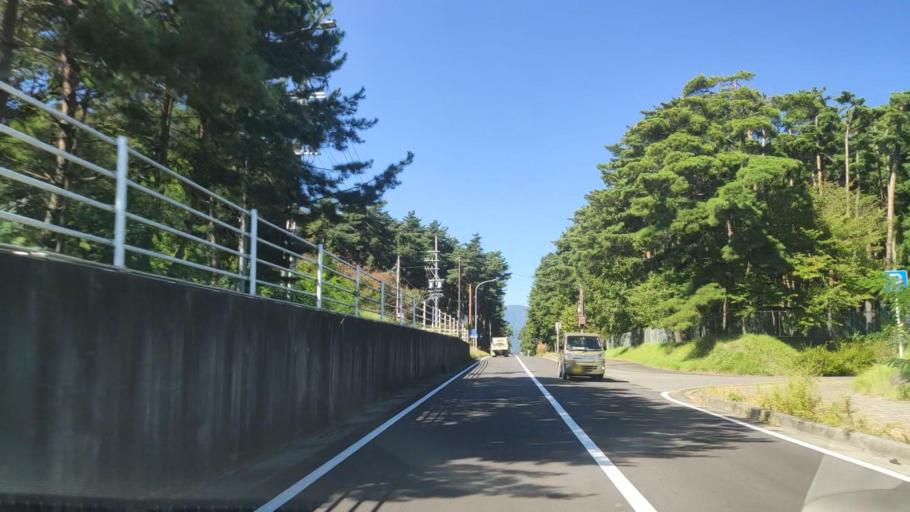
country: JP
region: Nagano
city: Shiojiri
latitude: 36.1630
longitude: 137.9228
